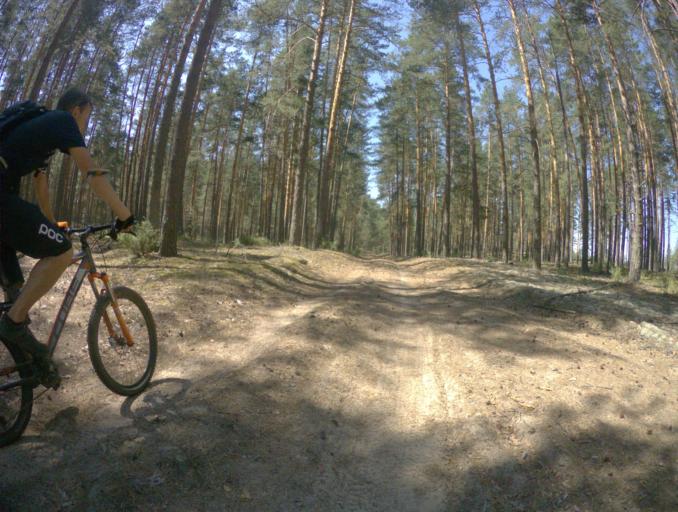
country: RU
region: Ivanovo
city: Talitsy
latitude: 56.3820
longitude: 42.3184
